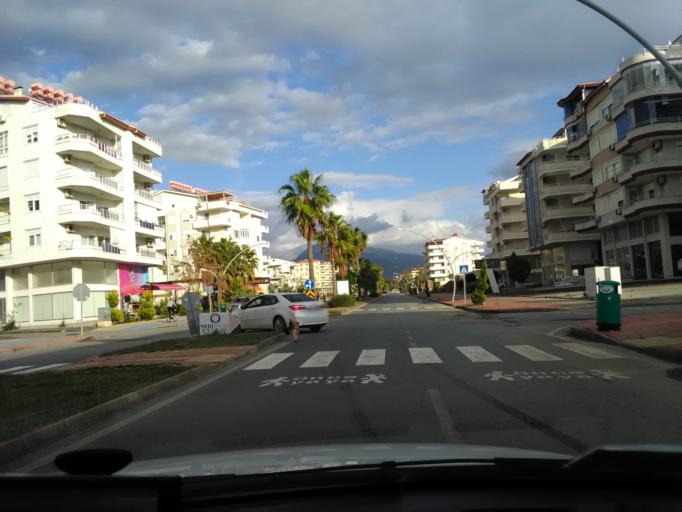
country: TR
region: Antalya
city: Gazipasa
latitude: 36.2664
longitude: 32.3011
